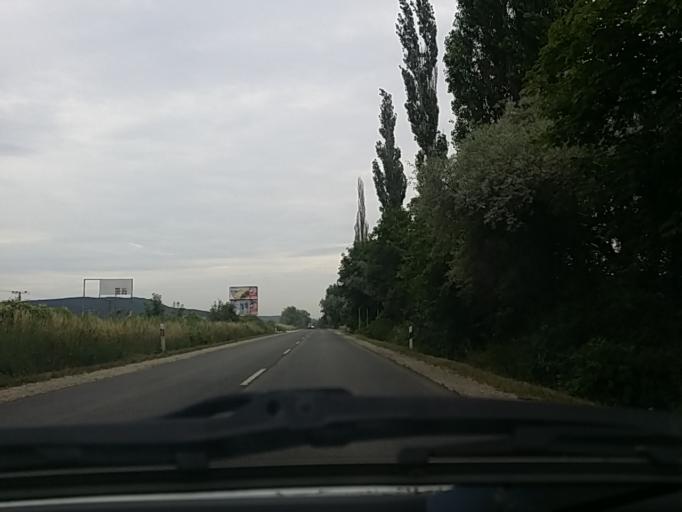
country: HU
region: Pest
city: Solymar
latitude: 47.6047
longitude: 18.9501
